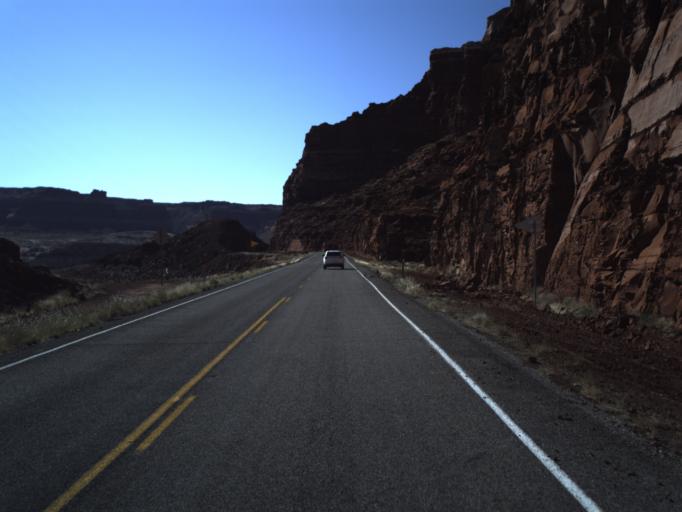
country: US
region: Utah
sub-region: San Juan County
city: Blanding
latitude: 37.8973
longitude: -110.3984
